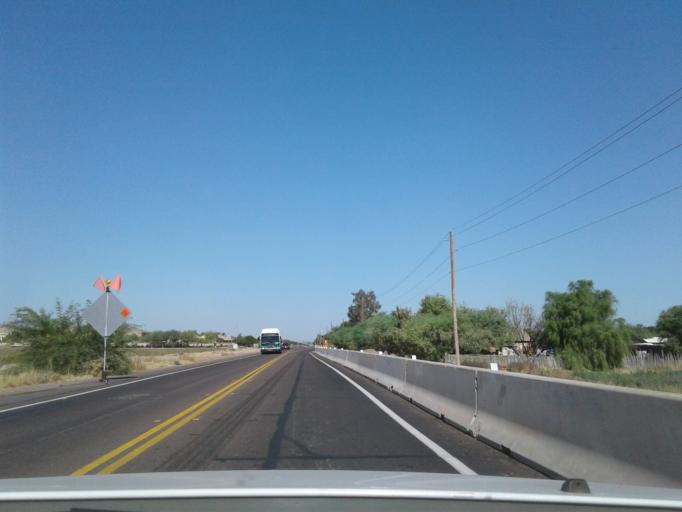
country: US
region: Arizona
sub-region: Maricopa County
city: Laveen
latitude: 33.3774
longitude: -112.1920
